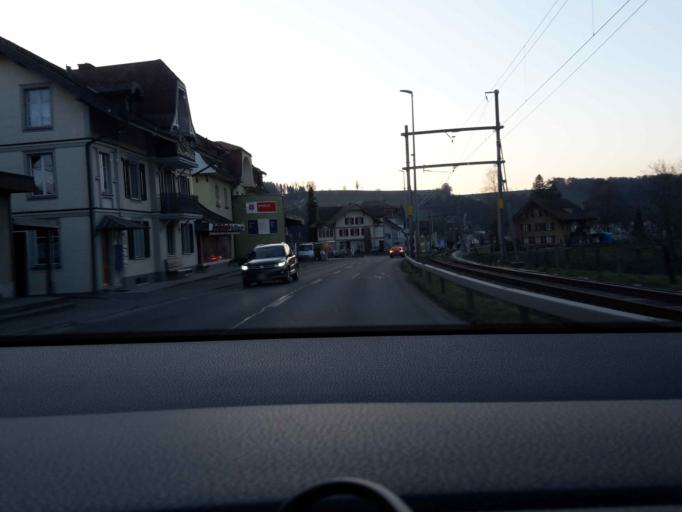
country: CH
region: Bern
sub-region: Oberaargau
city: Huttwil
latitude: 47.1147
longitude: 7.8392
